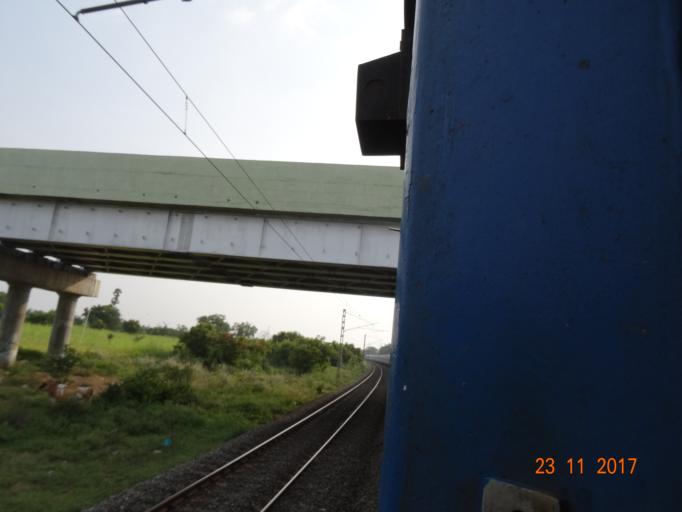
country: IN
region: Tamil Nadu
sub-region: Tiruppur
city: Tiruppur
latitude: 11.1285
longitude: 77.3696
